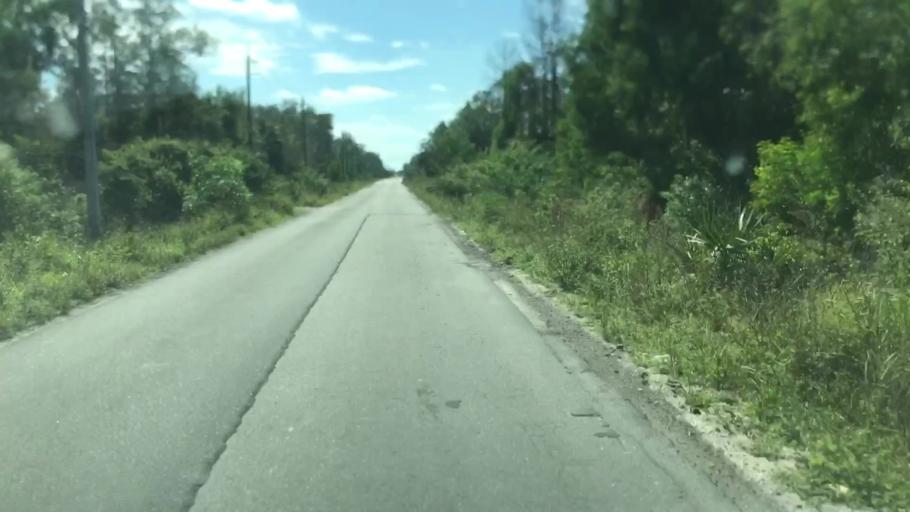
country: US
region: Florida
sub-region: Lee County
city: Bonita Springs
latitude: 26.3484
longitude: -81.7387
